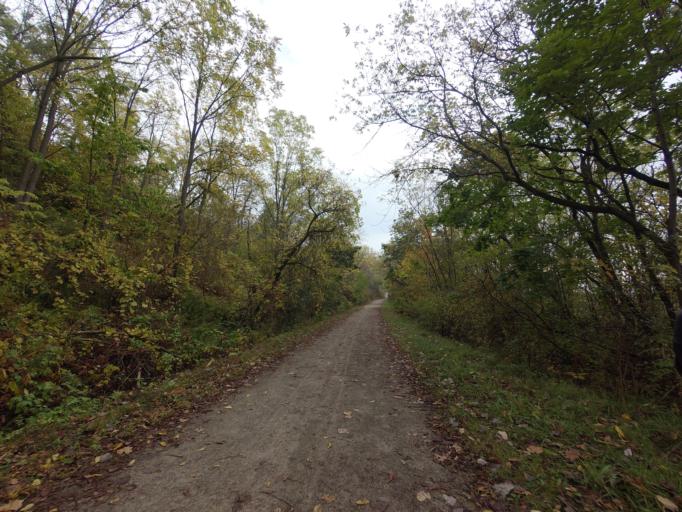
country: CA
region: Ontario
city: Brantford
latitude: 43.1441
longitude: -80.2118
